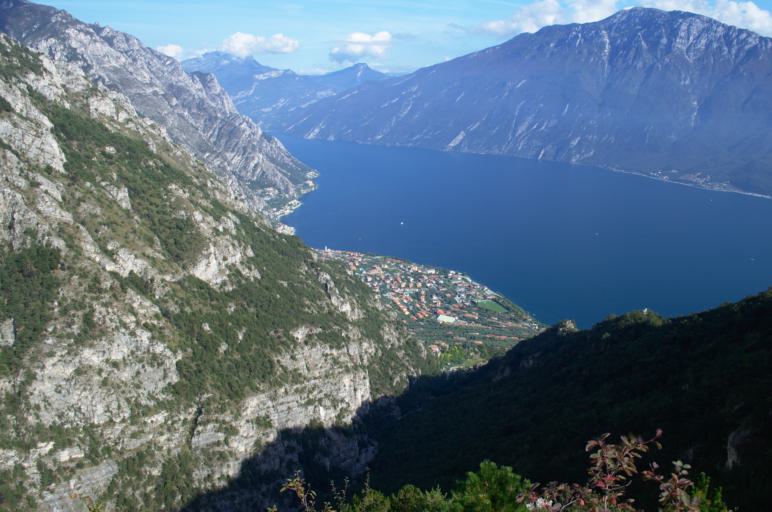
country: IT
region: Lombardy
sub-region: Provincia di Brescia
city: Pieve
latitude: 45.8017
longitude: 10.7658
